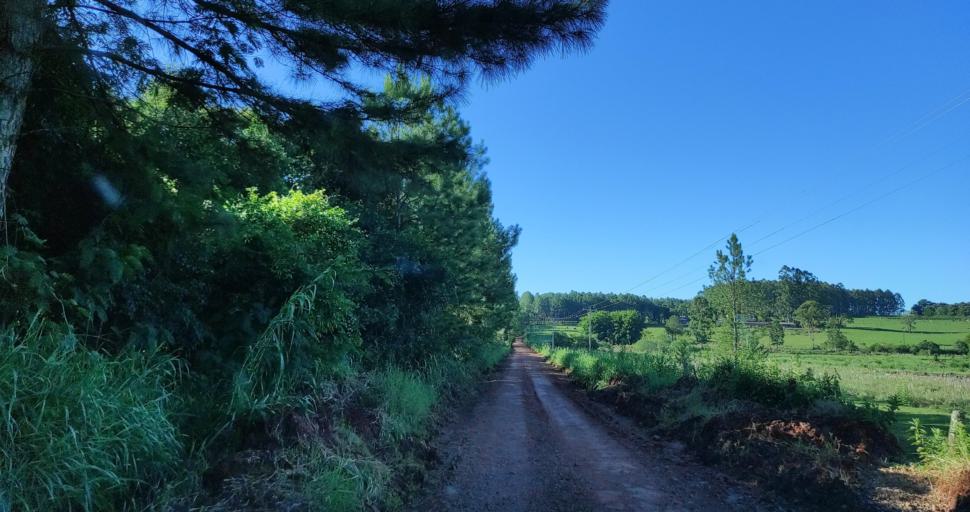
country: AR
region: Misiones
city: Puerto Rico
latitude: -26.8378
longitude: -55.0022
